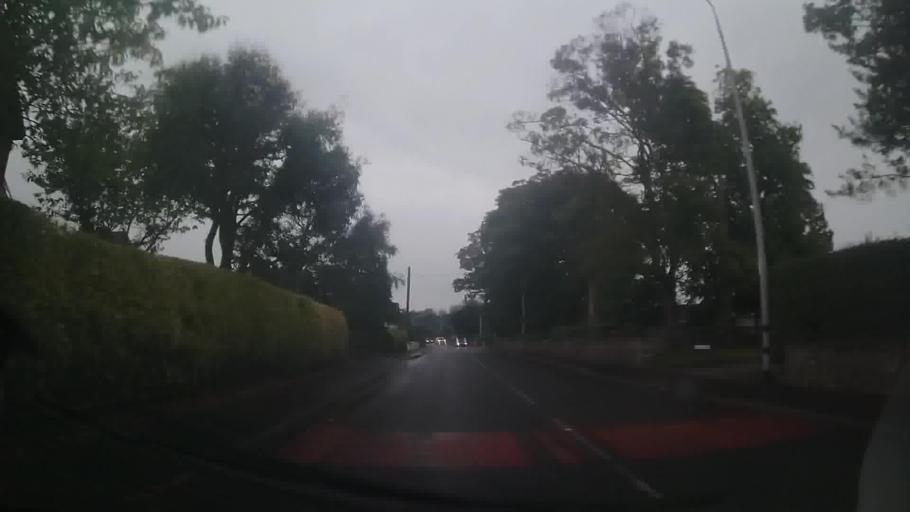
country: GB
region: Scotland
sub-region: North Ayrshire
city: Fairlie
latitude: 55.7527
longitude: -4.8558
